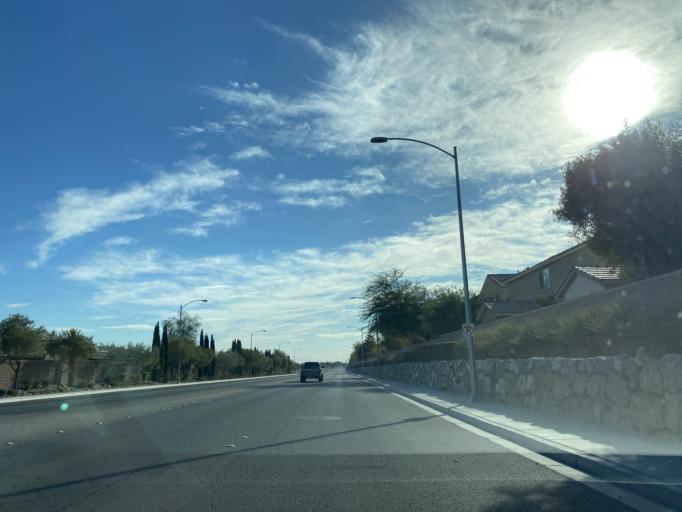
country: US
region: Nevada
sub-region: Clark County
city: North Las Vegas
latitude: 36.3113
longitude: -115.2423
